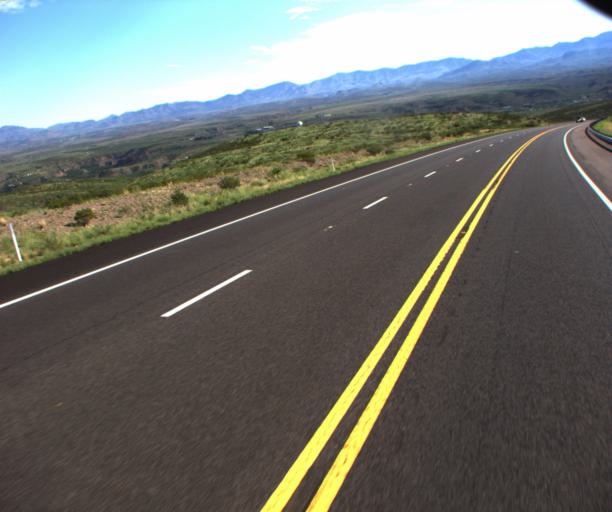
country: US
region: Arizona
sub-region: Greenlee County
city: Clifton
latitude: 32.9247
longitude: -109.2436
